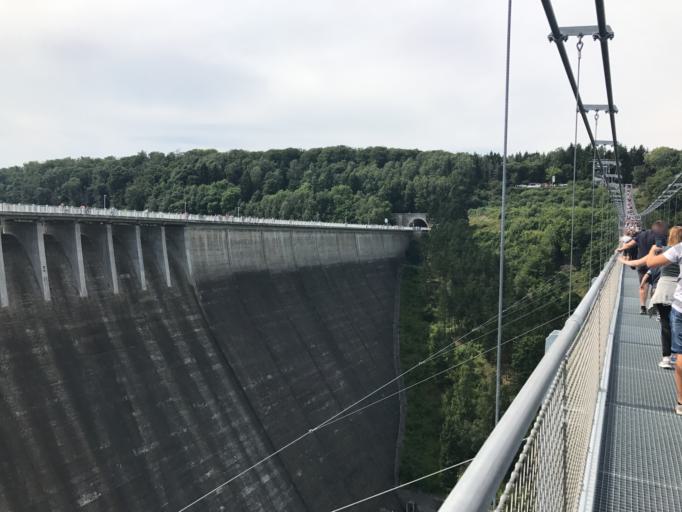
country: DE
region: Saxony-Anhalt
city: Huttenrode
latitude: 51.7403
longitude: 10.8948
